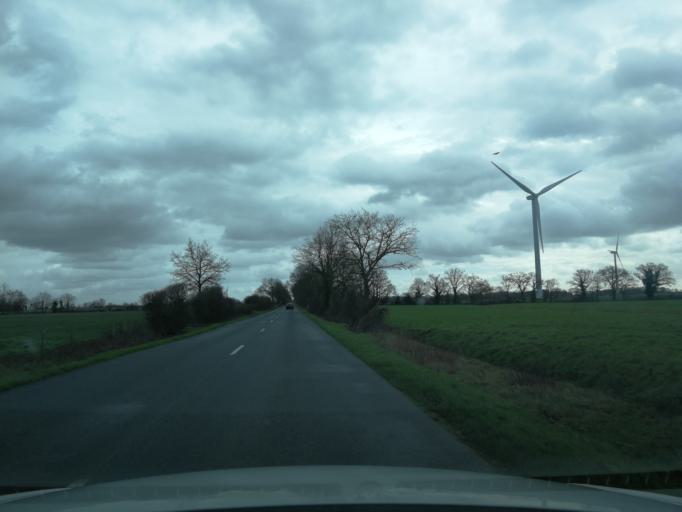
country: FR
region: Pays de la Loire
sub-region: Departement de la Loire-Atlantique
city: Montbert
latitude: 47.0118
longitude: -1.4794
